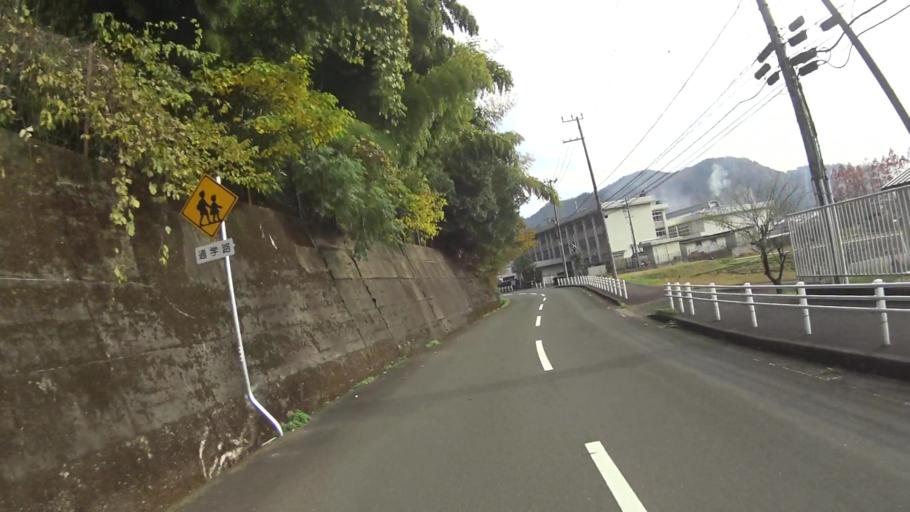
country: JP
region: Kyoto
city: Maizuru
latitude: 35.5189
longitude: 135.3950
